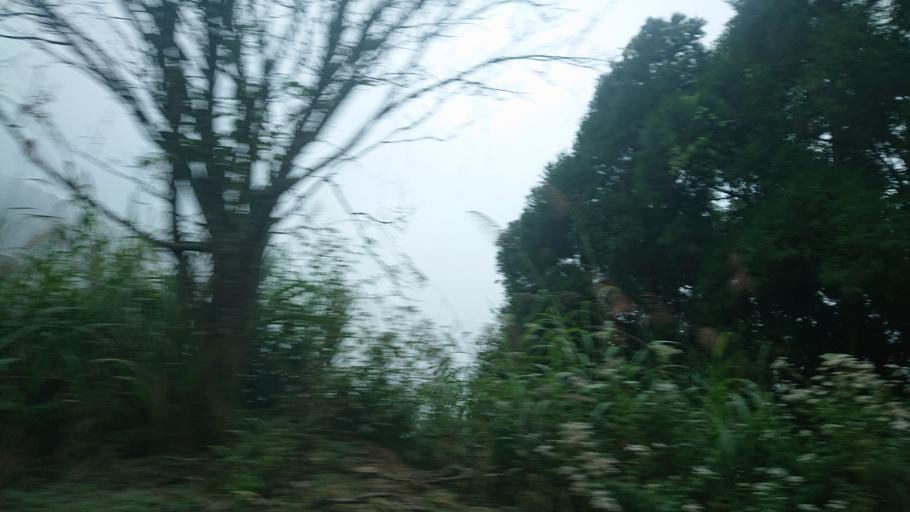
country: TW
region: Taiwan
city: Lugu
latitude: 23.6250
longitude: 120.7106
